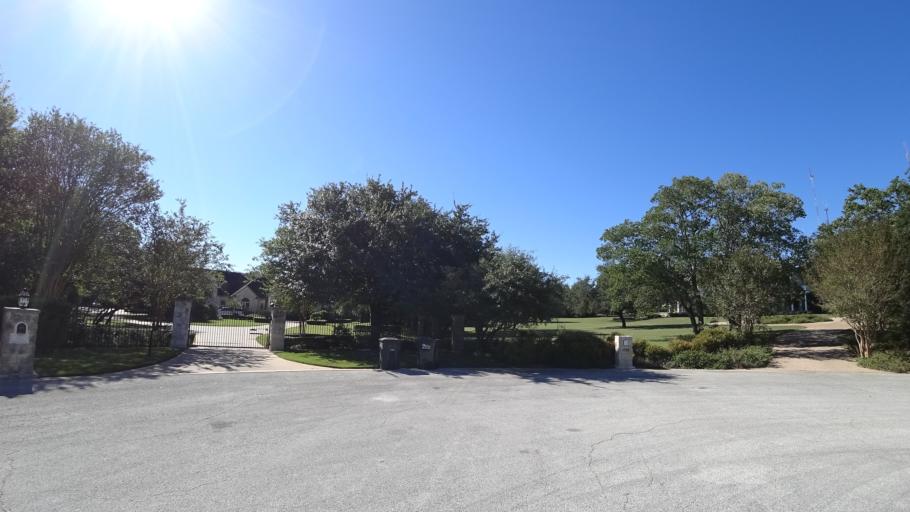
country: US
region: Texas
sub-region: Travis County
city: West Lake Hills
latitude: 30.3281
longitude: -97.7881
